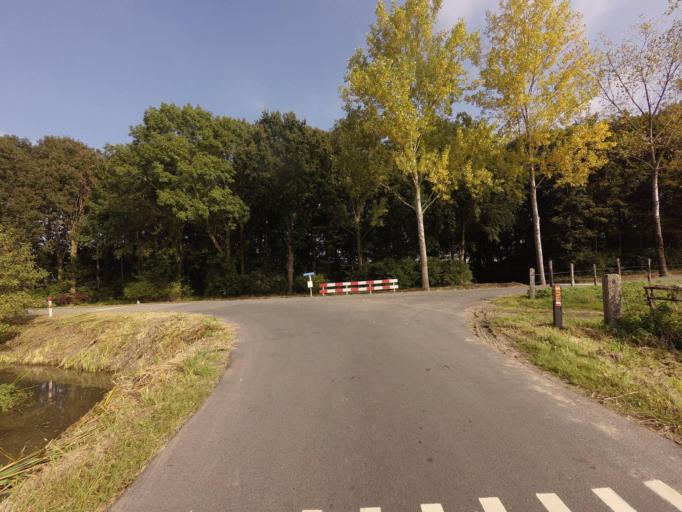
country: NL
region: Utrecht
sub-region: Gemeente Vianen
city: Vianen
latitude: 51.9712
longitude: 5.0898
